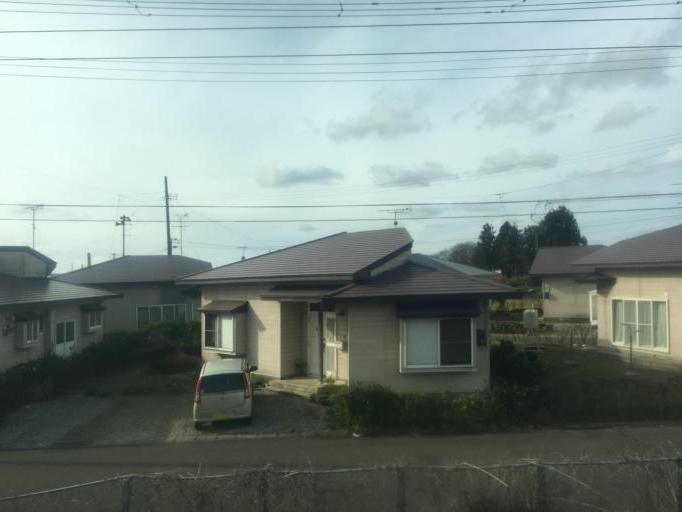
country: JP
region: Akita
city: Tenno
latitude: 39.9433
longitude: 140.0797
